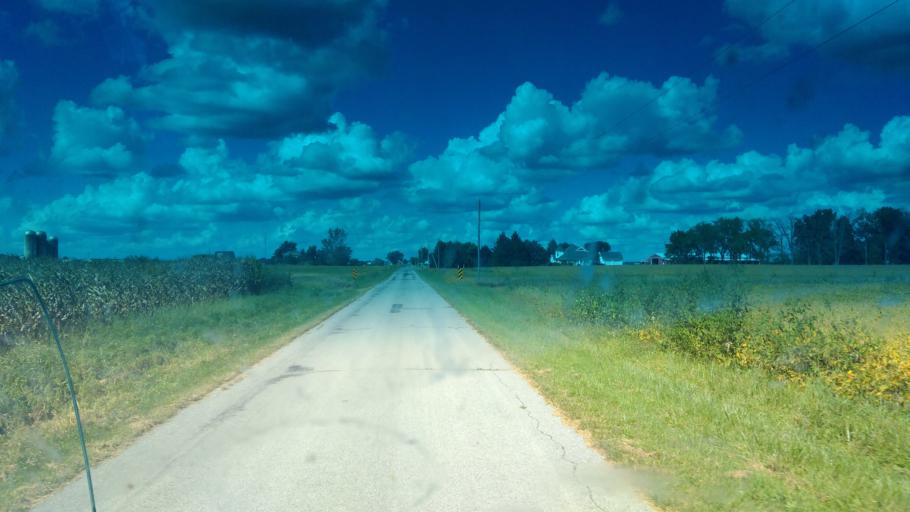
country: US
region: Ohio
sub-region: Hardin County
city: Kenton
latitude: 40.5144
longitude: -83.5399
